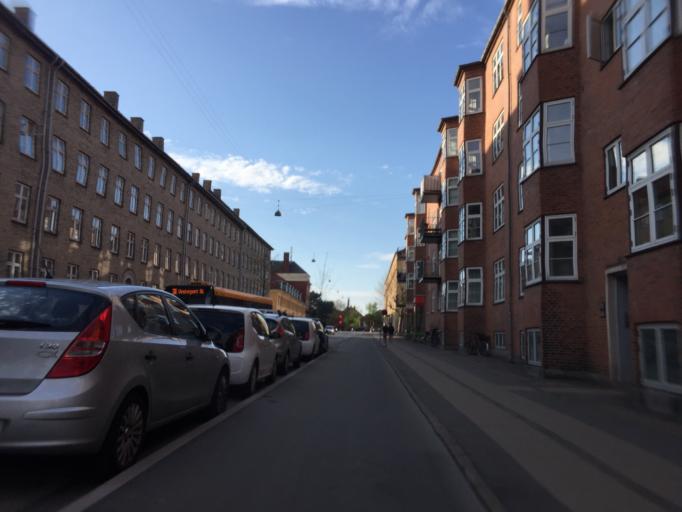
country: DK
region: Capital Region
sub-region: Kobenhavn
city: Vanlose
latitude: 55.6910
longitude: 12.4878
